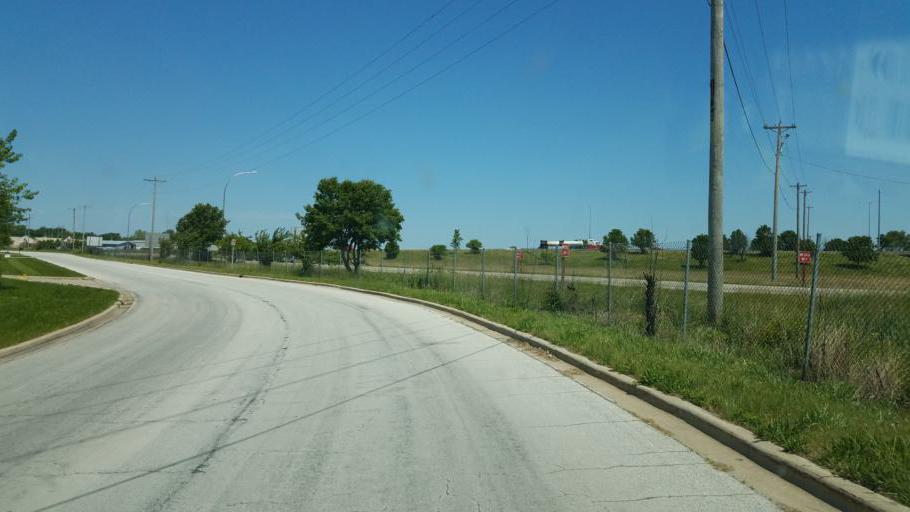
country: US
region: Illinois
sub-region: Champaign County
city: Urbana
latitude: 40.1321
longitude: -88.1971
